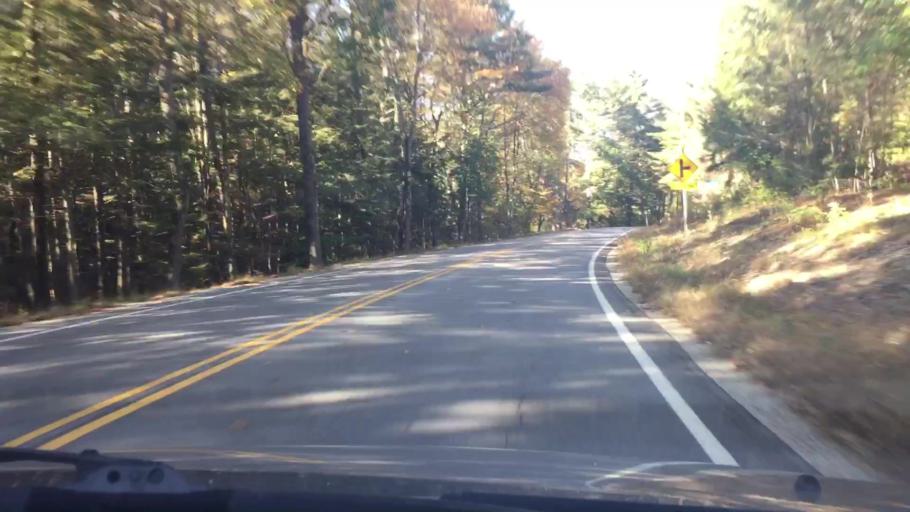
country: US
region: New Hampshire
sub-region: Cheshire County
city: Swanzey
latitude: 42.8409
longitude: -72.2796
